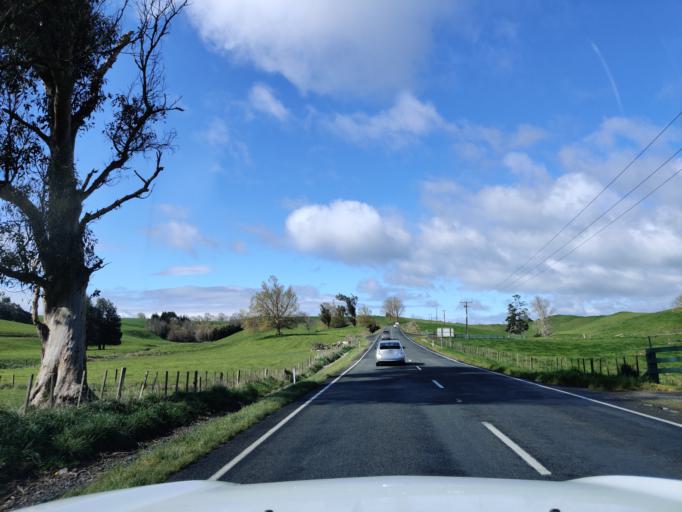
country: NZ
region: Waikato
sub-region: Otorohanga District
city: Otorohanga
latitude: -38.0897
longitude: 175.1821
